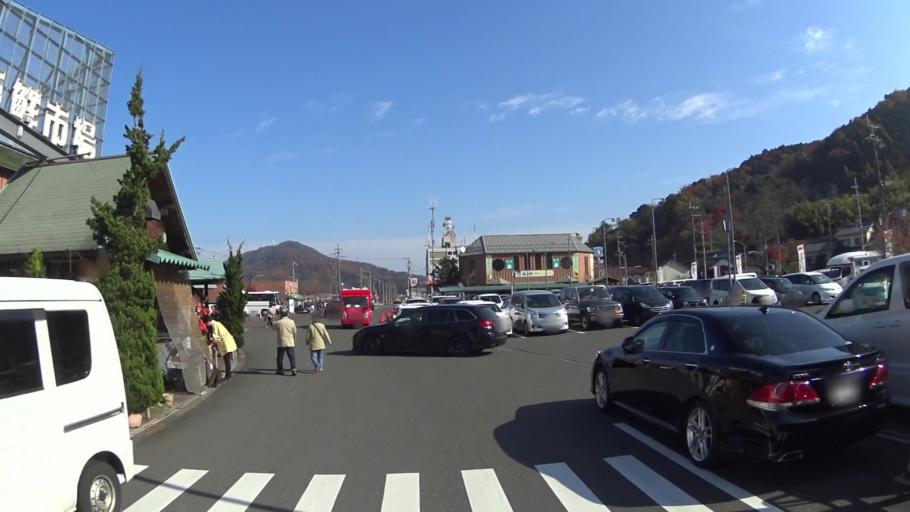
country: JP
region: Kyoto
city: Maizuru
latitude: 35.4501
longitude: 135.3147
